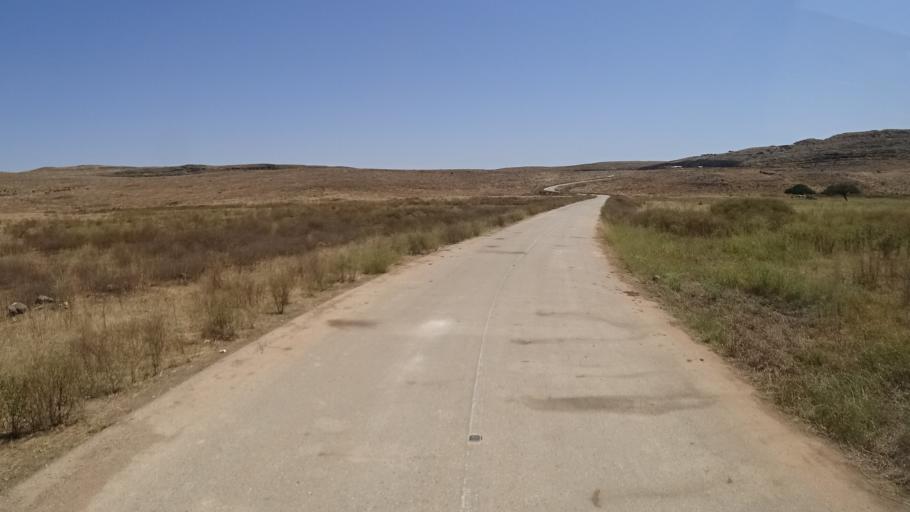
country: OM
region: Zufar
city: Salalah
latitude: 17.1550
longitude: 54.6182
